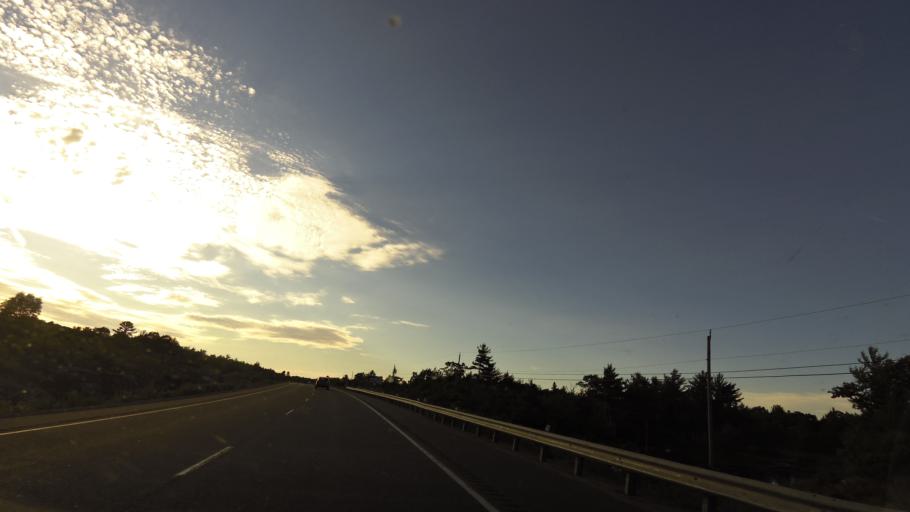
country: CA
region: Ontario
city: Midland
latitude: 44.8927
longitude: -79.7578
